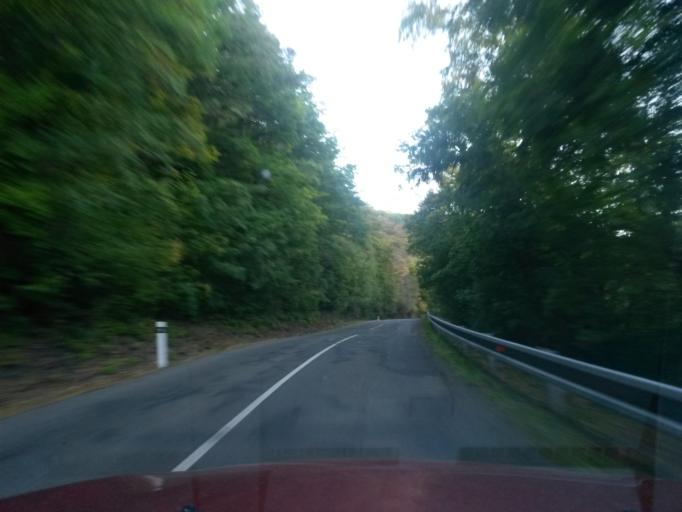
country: SK
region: Kosicky
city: Sobrance
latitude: 48.8015
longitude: 22.2691
